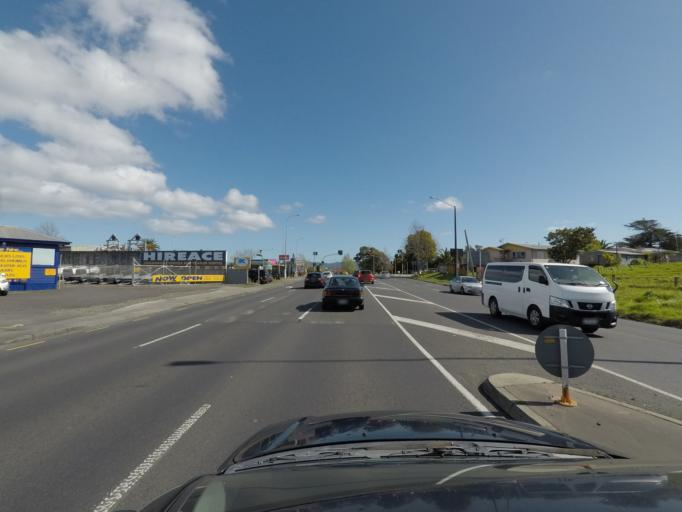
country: NZ
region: Auckland
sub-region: Auckland
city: Rosebank
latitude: -36.8505
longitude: 174.6313
